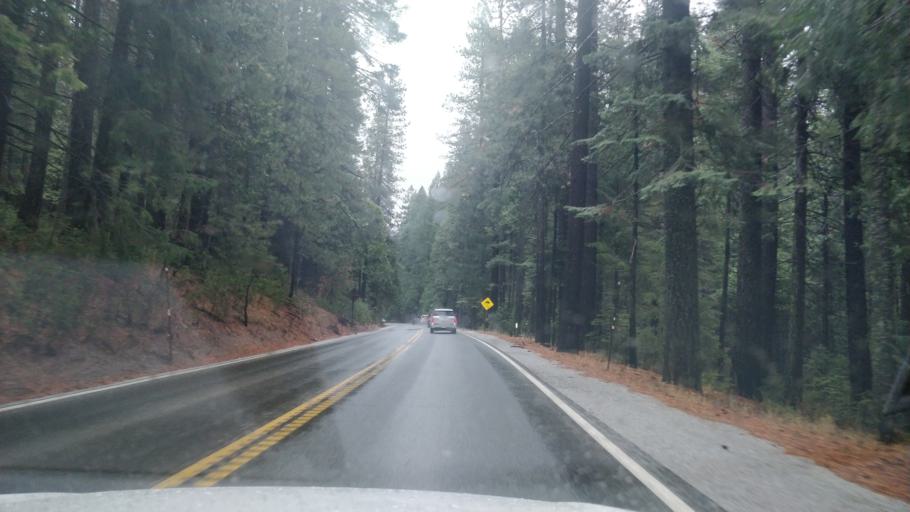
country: US
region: California
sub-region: Nevada County
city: Nevada City
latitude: 39.3152
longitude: -120.8058
